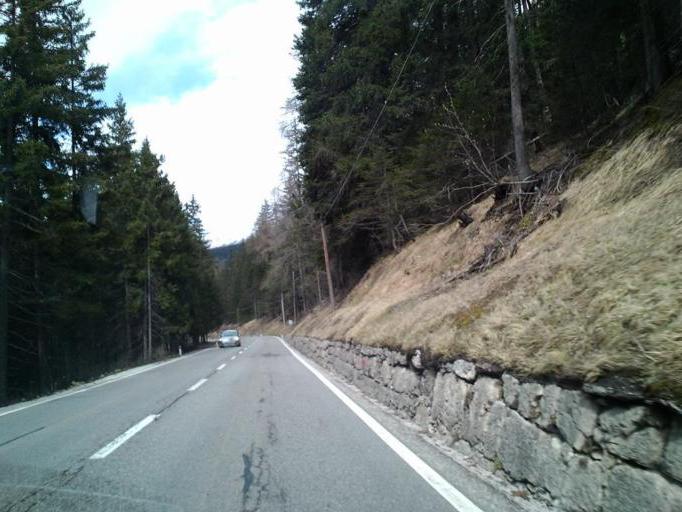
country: IT
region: Trentino-Alto Adige
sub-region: Bolzano
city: Dobbiaco
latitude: 46.7164
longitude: 12.2240
